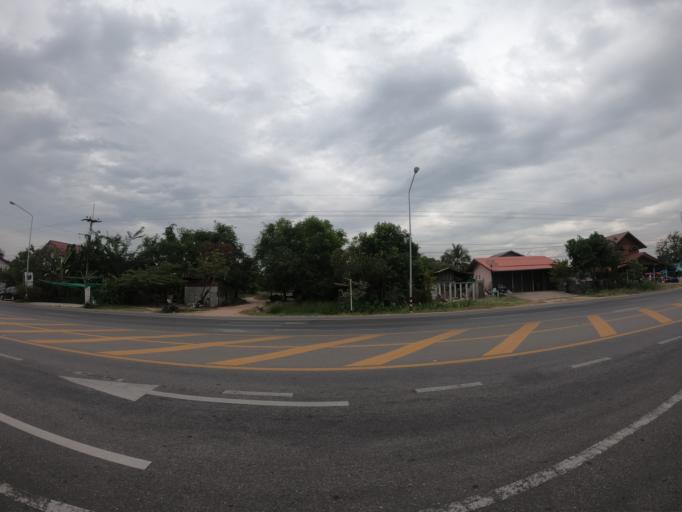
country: TH
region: Roi Et
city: Chiang Khwan
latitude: 16.1010
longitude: 103.8039
